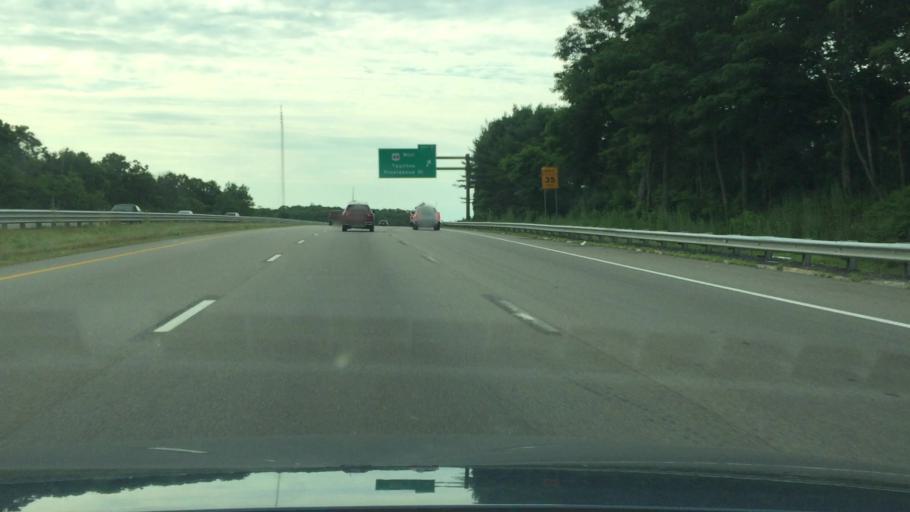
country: US
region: Massachusetts
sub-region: Plymouth County
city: North Plymouth
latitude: 41.9624
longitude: -70.6918
